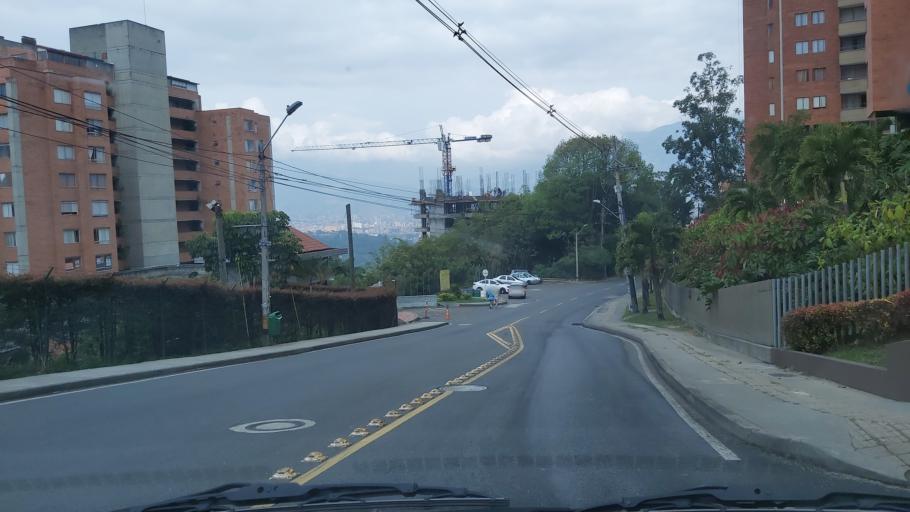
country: CO
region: Antioquia
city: Medellin
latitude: 6.2278
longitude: -75.5625
